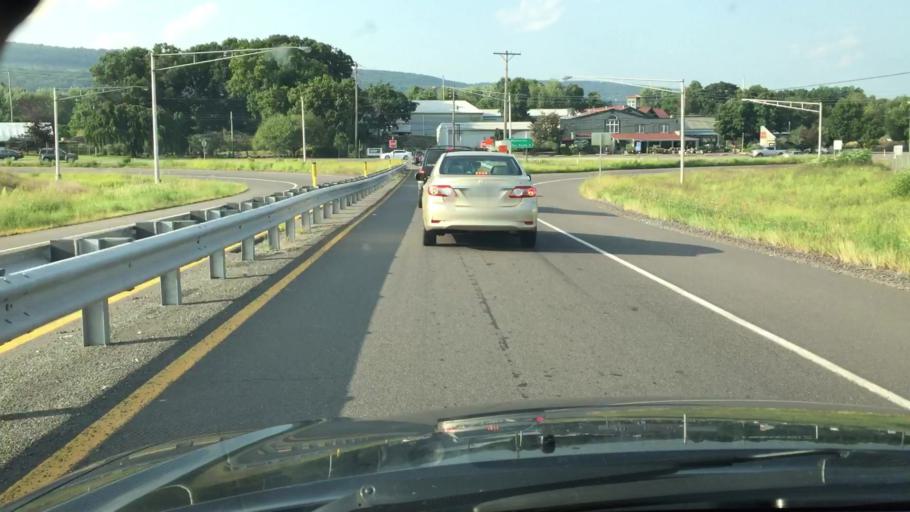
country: US
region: Pennsylvania
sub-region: Luzerne County
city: Nanticoke
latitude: 41.2080
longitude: -75.9784
